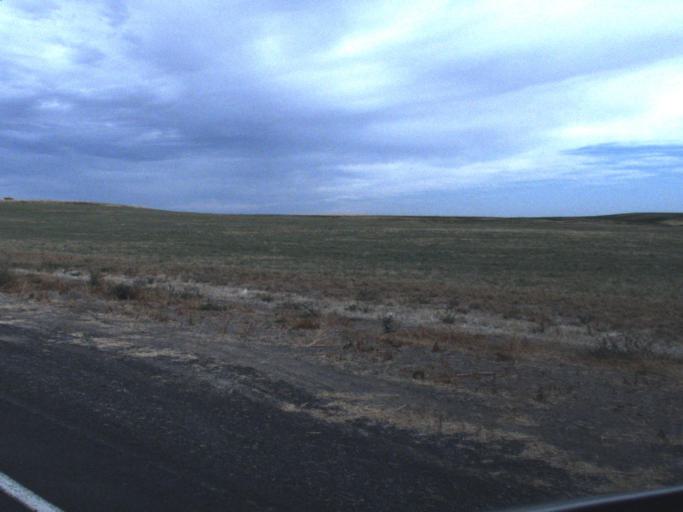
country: US
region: Washington
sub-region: Okanogan County
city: Coulee Dam
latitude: 47.4787
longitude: -118.7848
